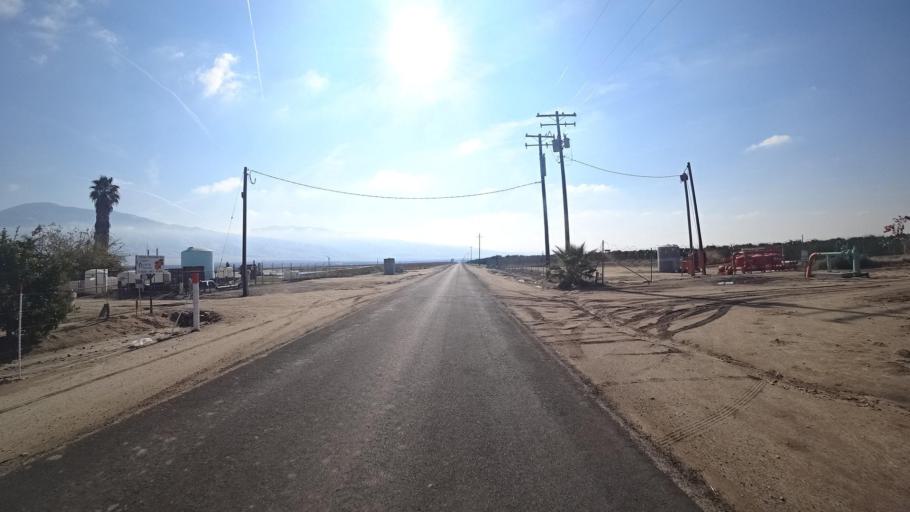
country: US
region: California
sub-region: Kern County
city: Arvin
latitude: 35.2751
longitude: -118.7708
